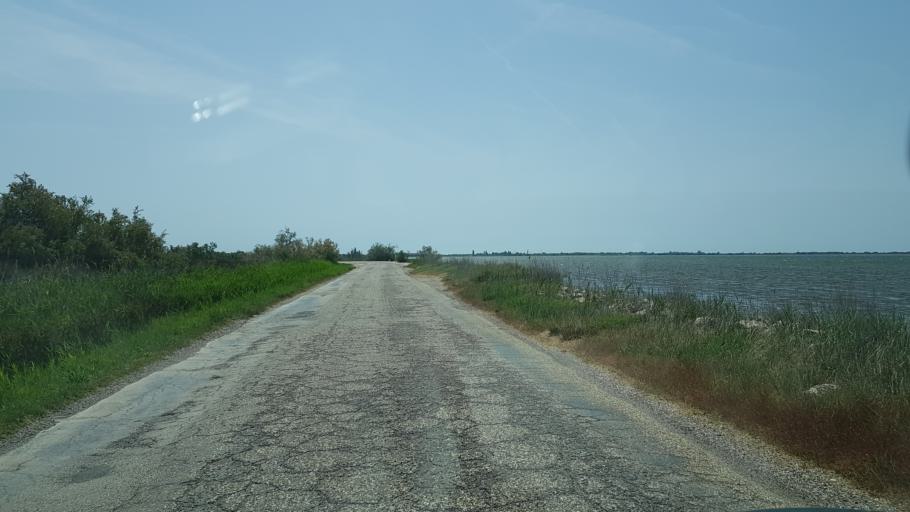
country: FR
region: Provence-Alpes-Cote d'Azur
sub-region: Departement des Bouches-du-Rhone
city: Arles
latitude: 43.5435
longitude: 4.6325
